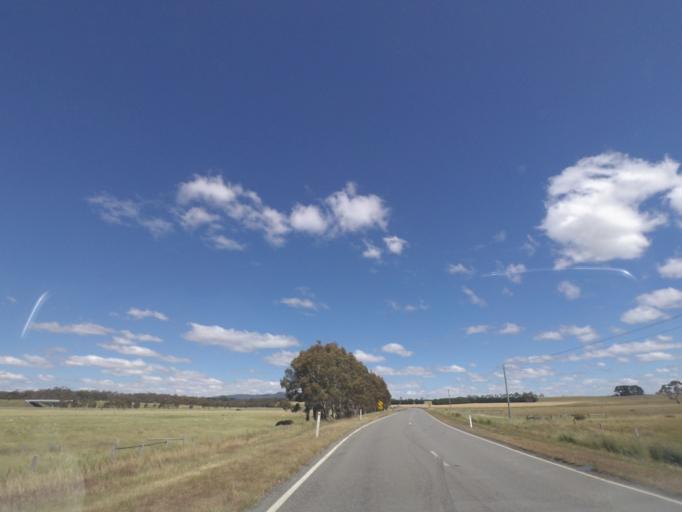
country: AU
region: Victoria
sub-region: Mount Alexander
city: Castlemaine
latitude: -37.2935
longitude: 144.4975
